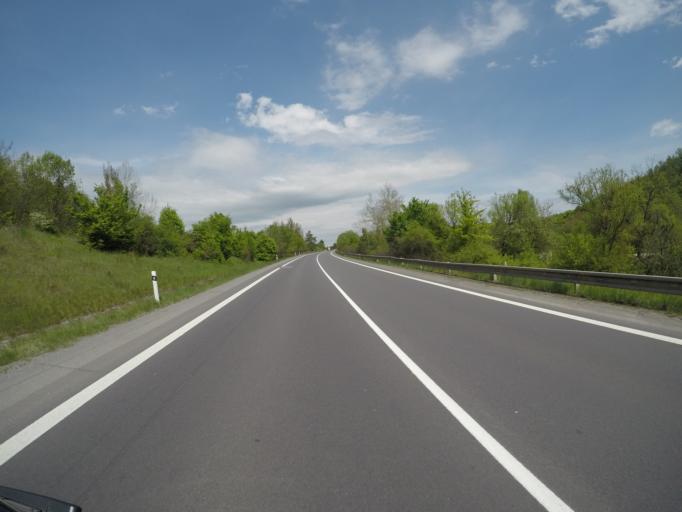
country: SK
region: Banskobystricky
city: Krupina
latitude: 48.4120
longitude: 19.0857
